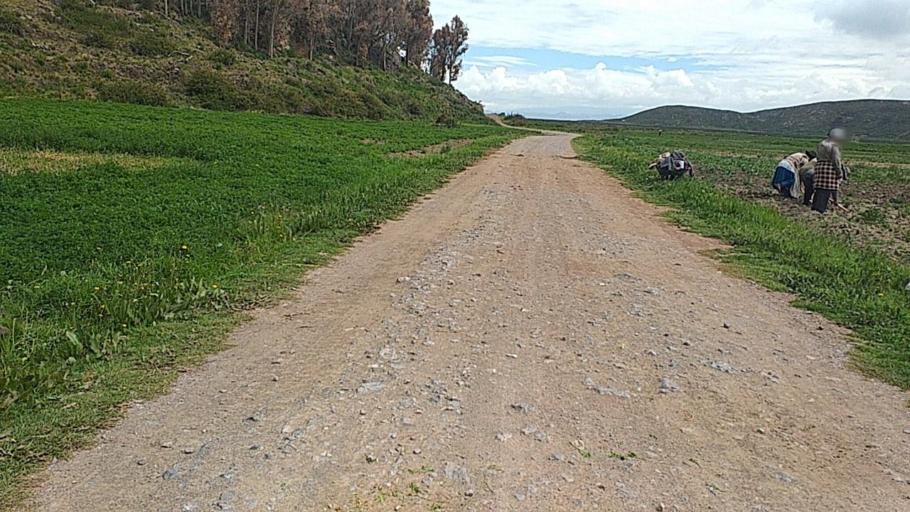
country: BO
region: La Paz
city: Batallas
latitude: -16.3457
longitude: -68.6349
